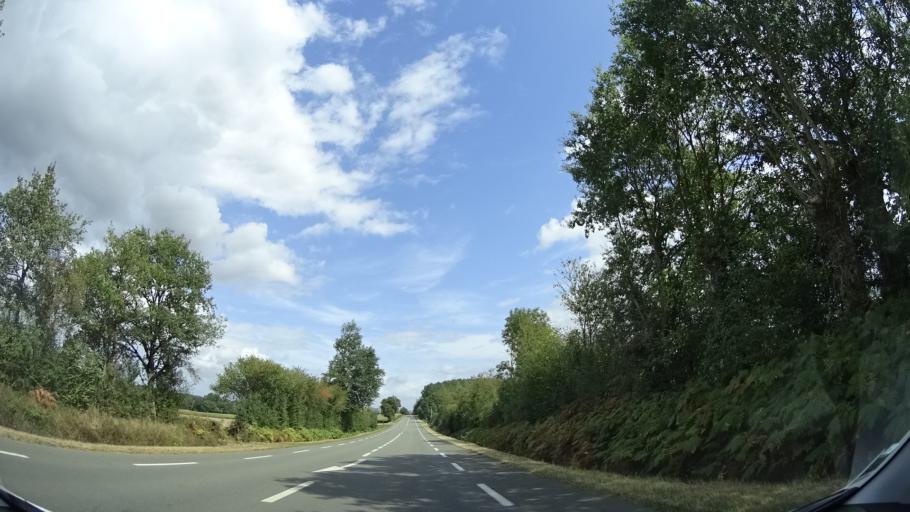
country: FR
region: Pays de la Loire
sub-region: Departement de la Mayenne
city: Vaiges
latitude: 48.0376
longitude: -0.4214
